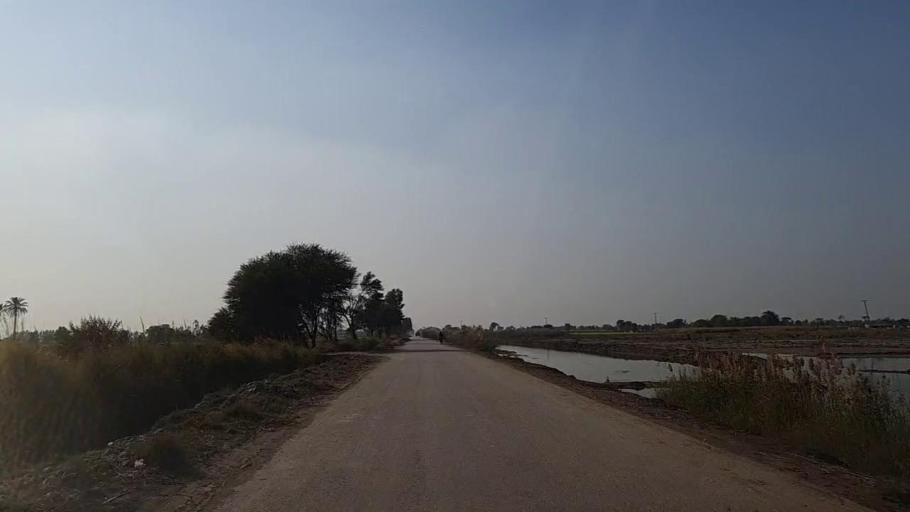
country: PK
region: Sindh
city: Daur
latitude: 26.4042
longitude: 68.2730
